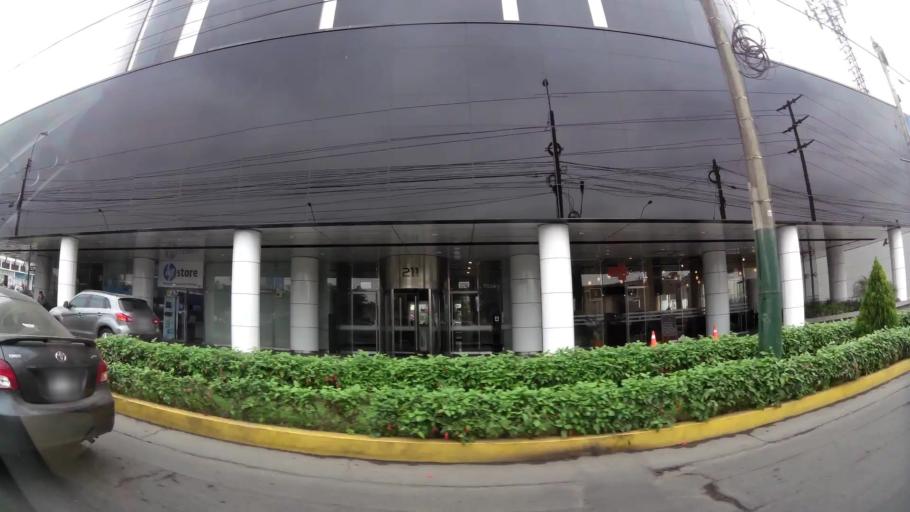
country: PE
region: Lima
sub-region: Lima
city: San Luis
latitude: -12.0856
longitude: -76.9731
